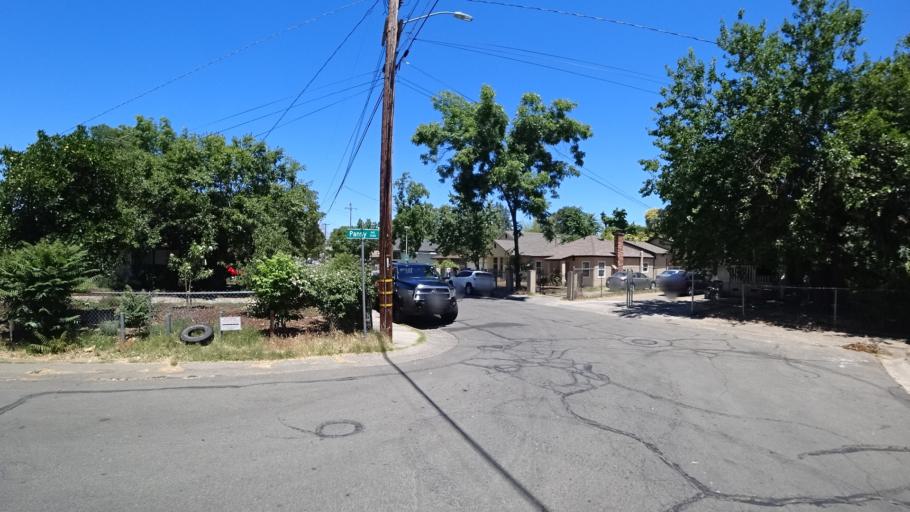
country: US
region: California
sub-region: Sacramento County
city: Sacramento
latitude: 38.5431
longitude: -121.4673
